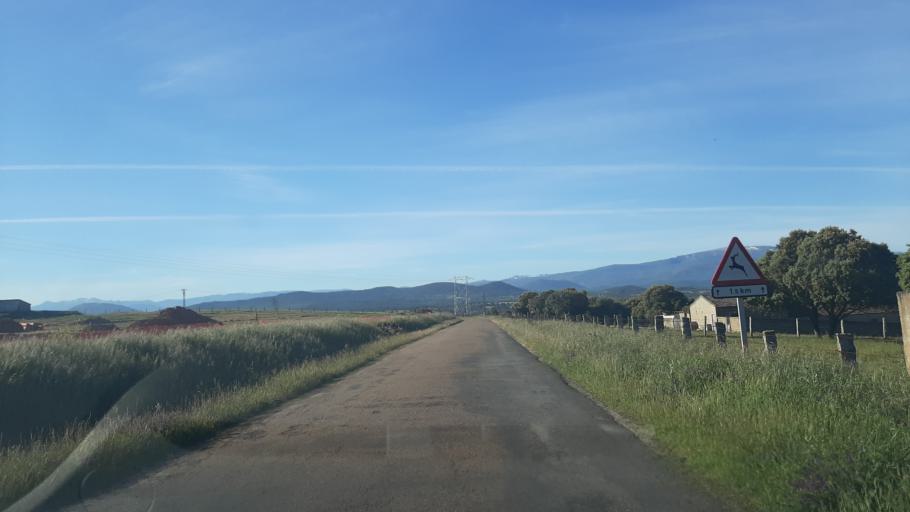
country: ES
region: Castille and Leon
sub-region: Provincia de Salamanca
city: Guijuelo
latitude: 40.5499
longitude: -5.6661
